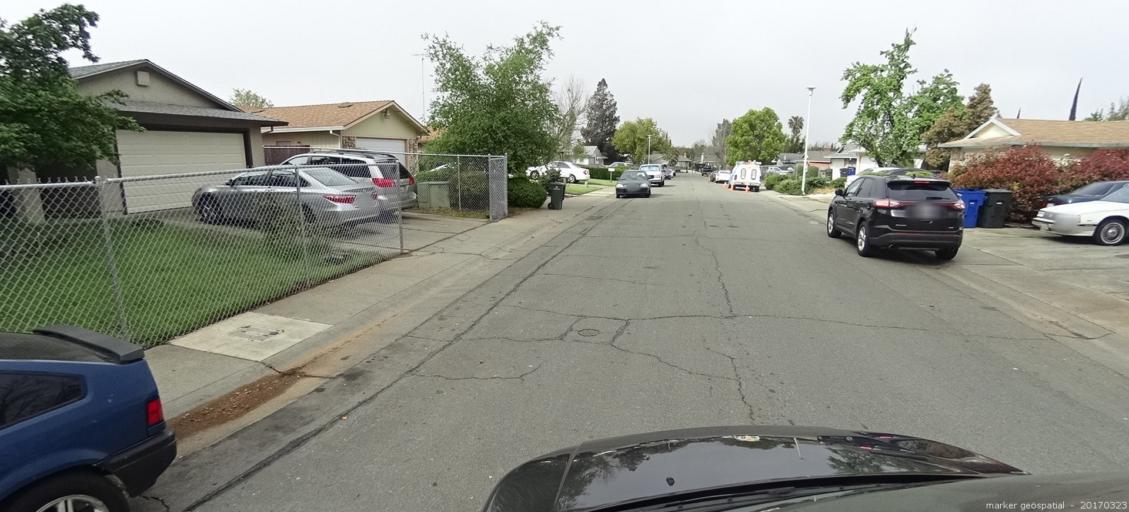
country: US
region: California
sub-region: Sacramento County
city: Florin
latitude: 38.5123
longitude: -121.4162
